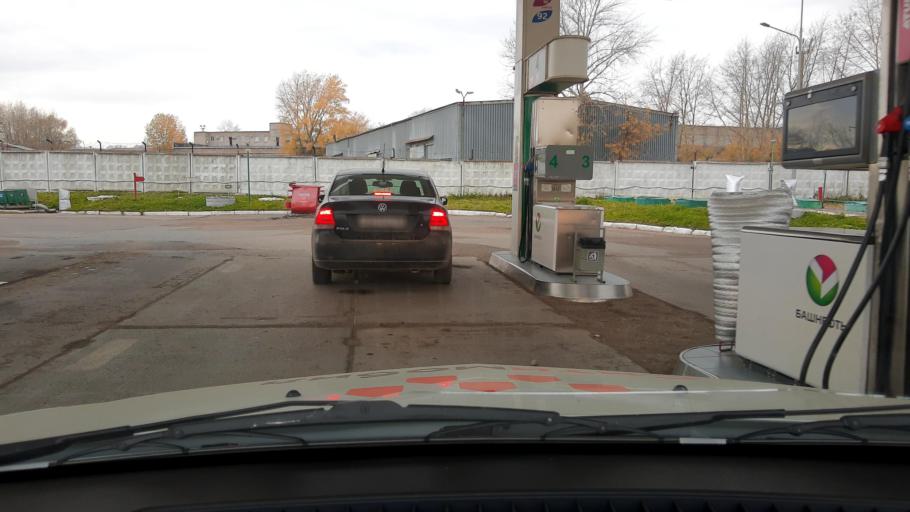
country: RU
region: Bashkortostan
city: Ufa
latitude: 54.8289
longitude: 56.1202
